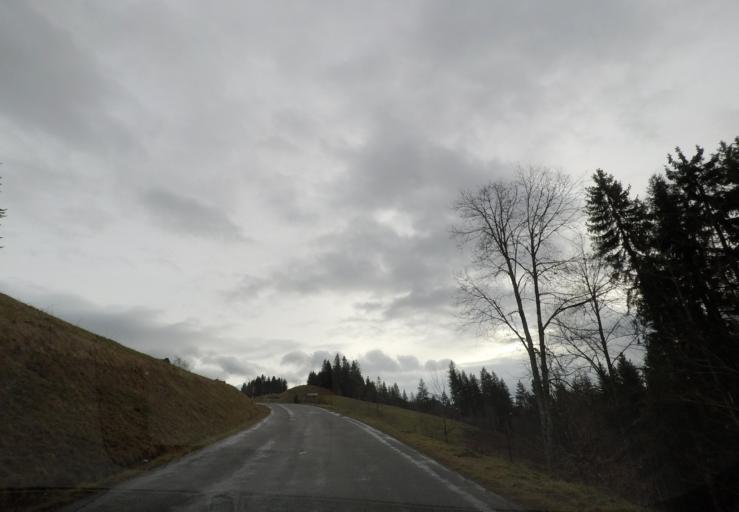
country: FR
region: Rhone-Alpes
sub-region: Departement de la Haute-Savoie
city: Chatillon-sur-Cluses
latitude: 46.0795
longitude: 6.6189
